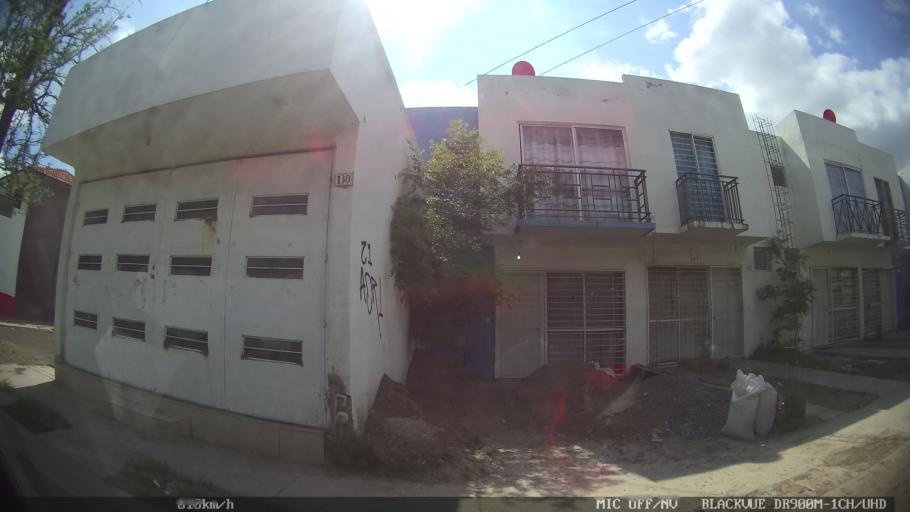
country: MX
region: Jalisco
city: Tonala
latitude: 20.6604
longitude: -103.2439
